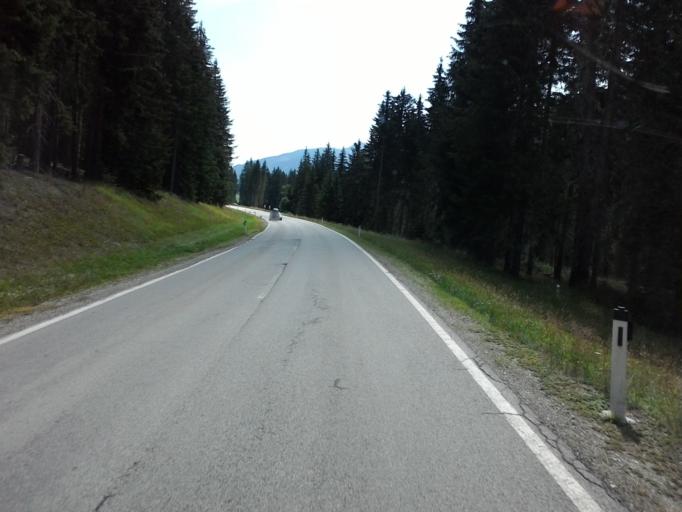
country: AT
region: Tyrol
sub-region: Politischer Bezirk Lienz
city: Obertilliach
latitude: 46.7105
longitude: 12.5817
